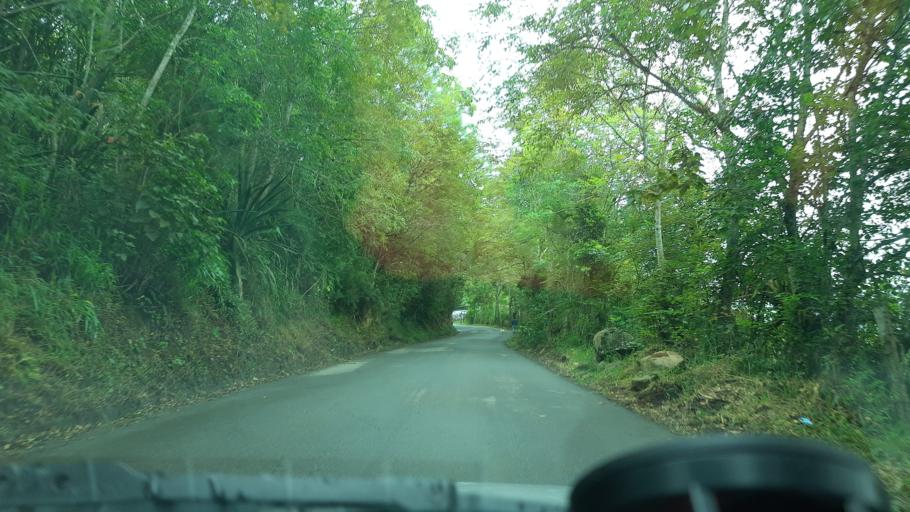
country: CO
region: Boyaca
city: Chinavita
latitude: 5.1716
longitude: -73.3731
